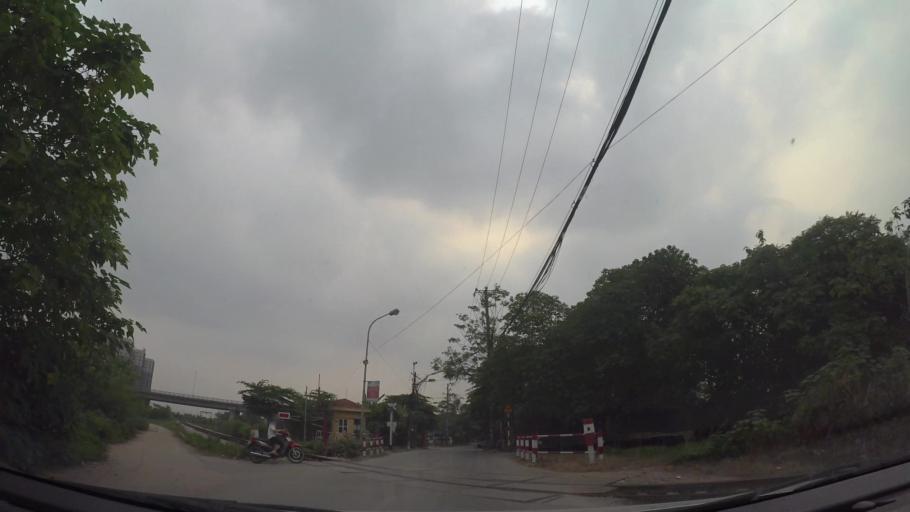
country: VN
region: Ha Noi
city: Cau Dien
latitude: 21.0357
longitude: 105.7533
